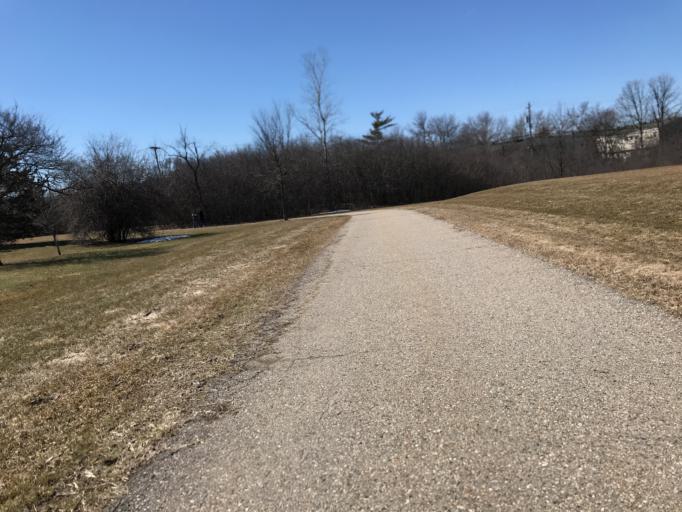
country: US
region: Michigan
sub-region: Washtenaw County
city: Ann Arbor
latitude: 42.2321
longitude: -83.7038
